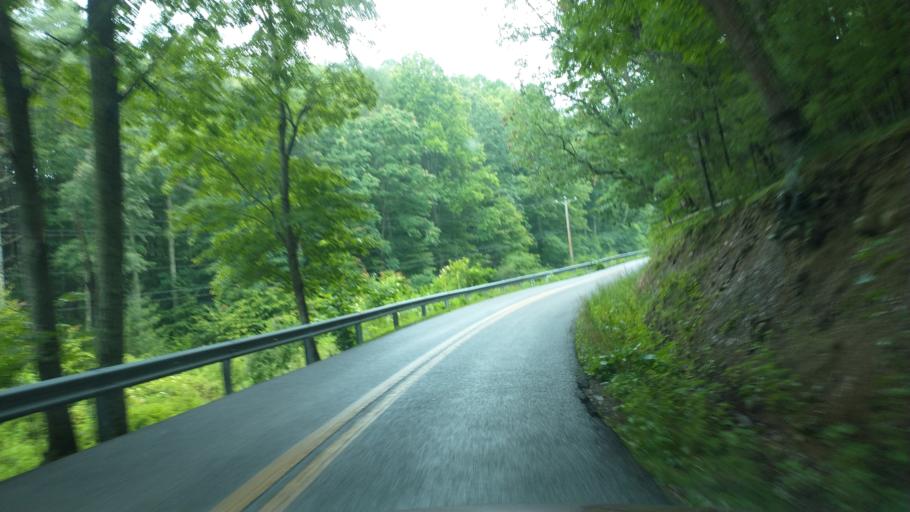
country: US
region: West Virginia
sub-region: Mercer County
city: Athens
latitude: 37.4343
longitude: -80.9666
